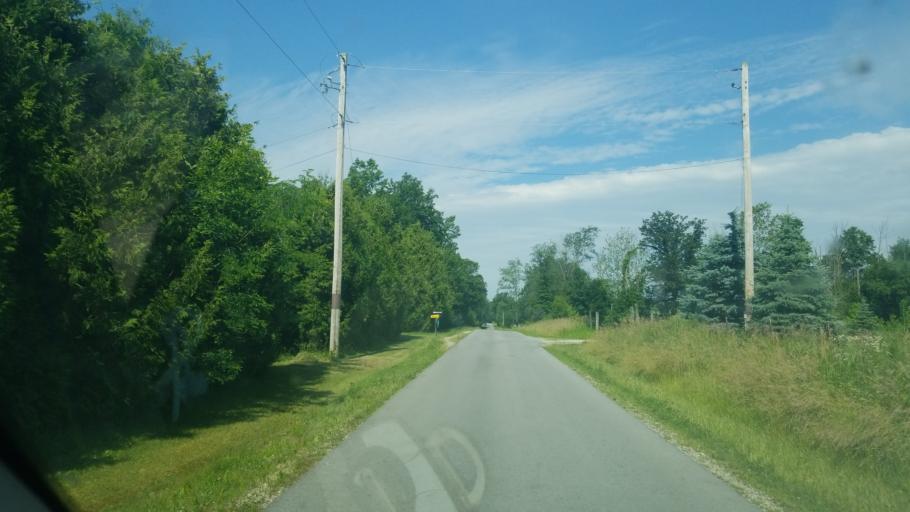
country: US
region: Ohio
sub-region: Wyandot County
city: Carey
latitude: 40.9564
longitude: -83.2909
